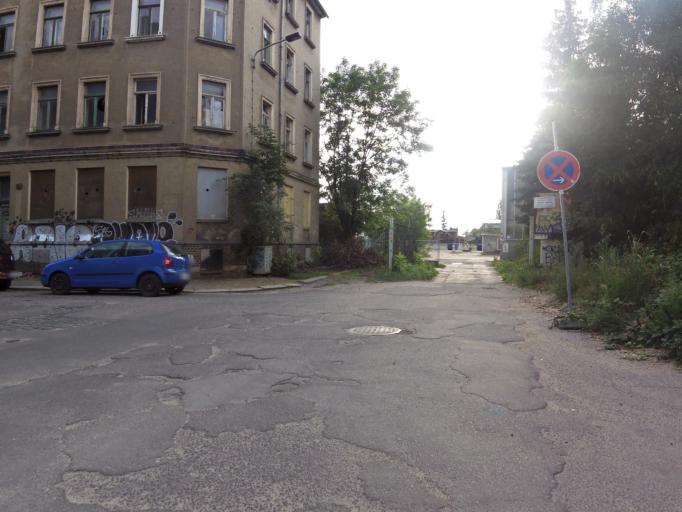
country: DE
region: Saxony
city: Leipzig
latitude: 51.3164
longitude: 12.3212
